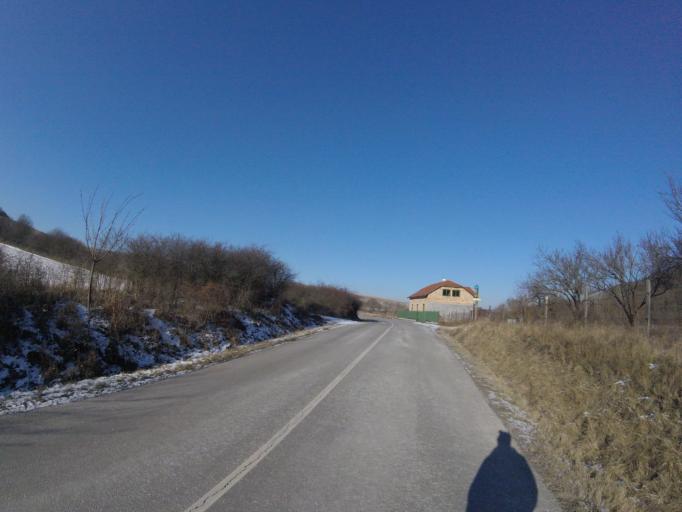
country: HU
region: Nograd
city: Tar
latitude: 47.9948
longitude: 19.7153
